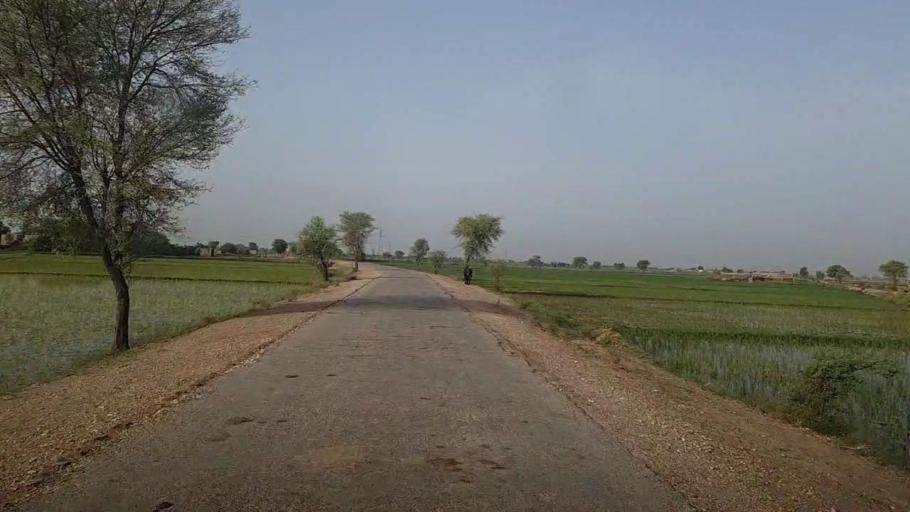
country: PK
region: Sindh
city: Mehar
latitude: 27.1469
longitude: 67.7967
